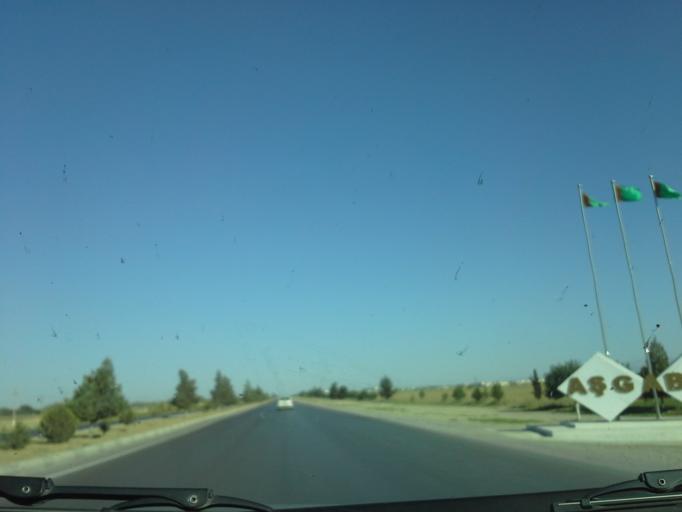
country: TM
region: Ahal
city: Abadan
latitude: 38.0831
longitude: 58.1231
